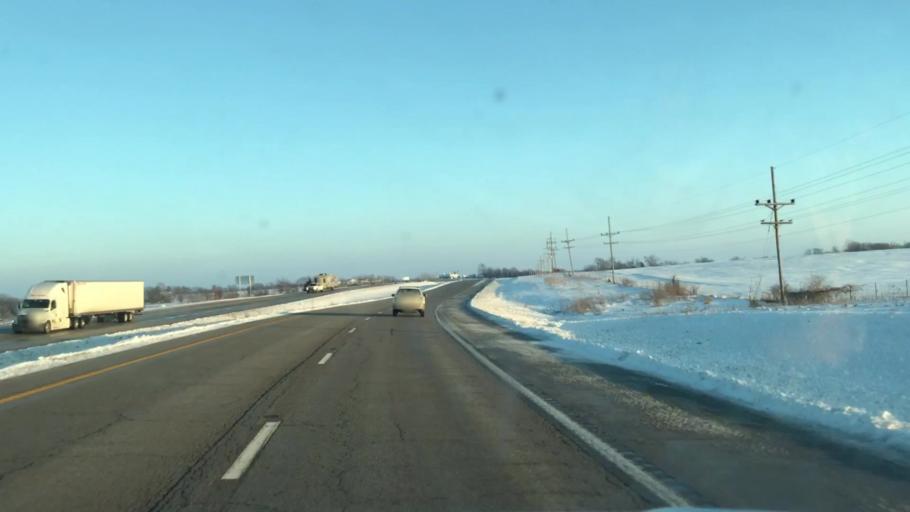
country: US
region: Missouri
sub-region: Clinton County
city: Cameron
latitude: 39.7605
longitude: -94.3497
